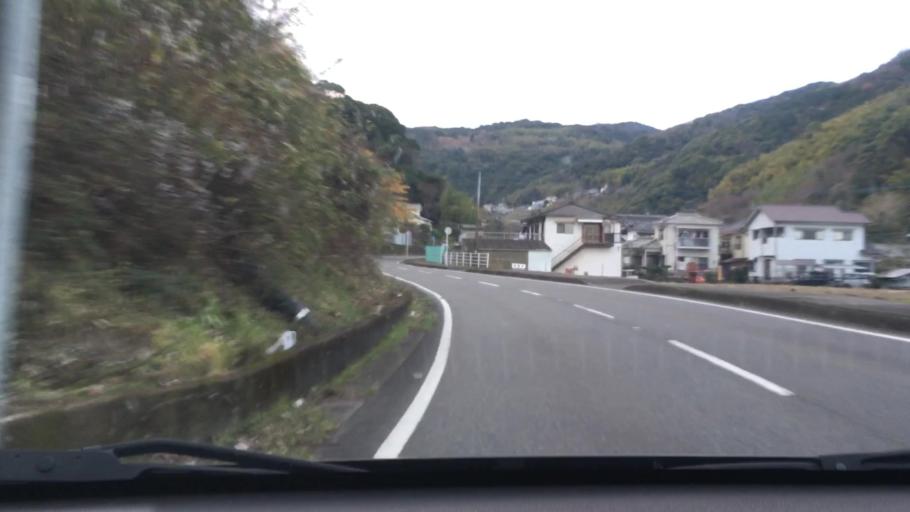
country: JP
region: Oita
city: Hiji
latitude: 33.3602
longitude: 131.4932
